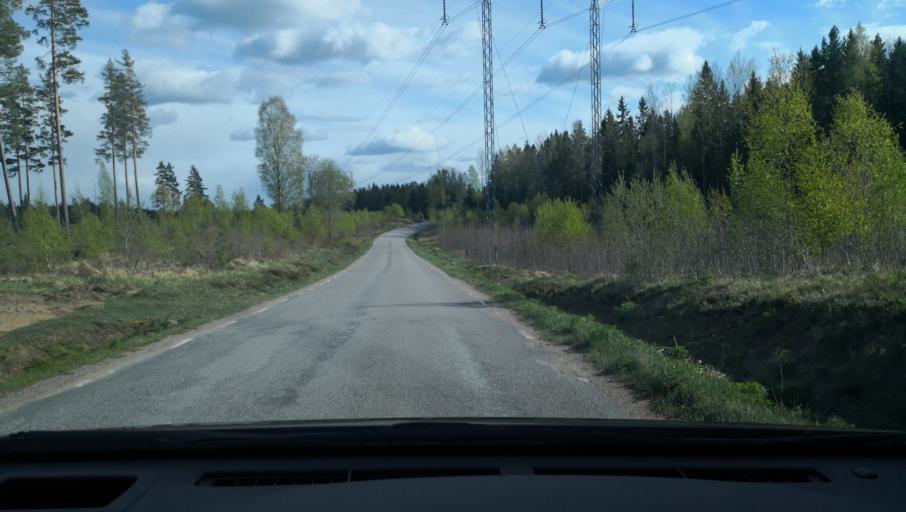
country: SE
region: OErebro
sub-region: Askersunds Kommun
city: Asbro
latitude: 58.9675
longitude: 15.0685
